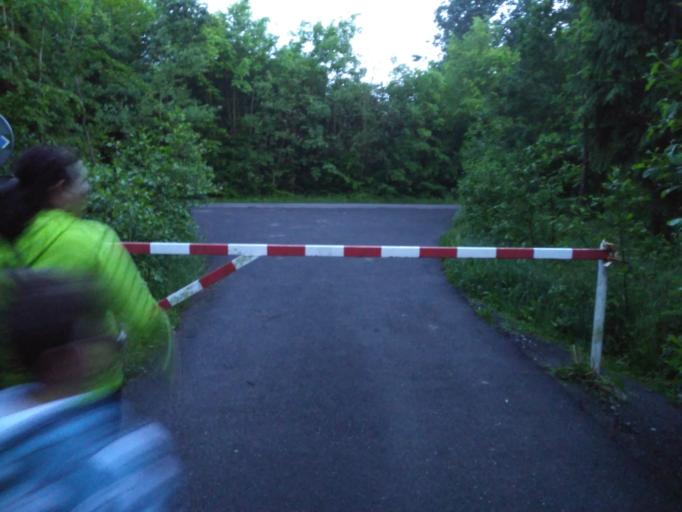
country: CZ
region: Central Bohemia
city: Hudlice
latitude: 49.9557
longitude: 13.9242
